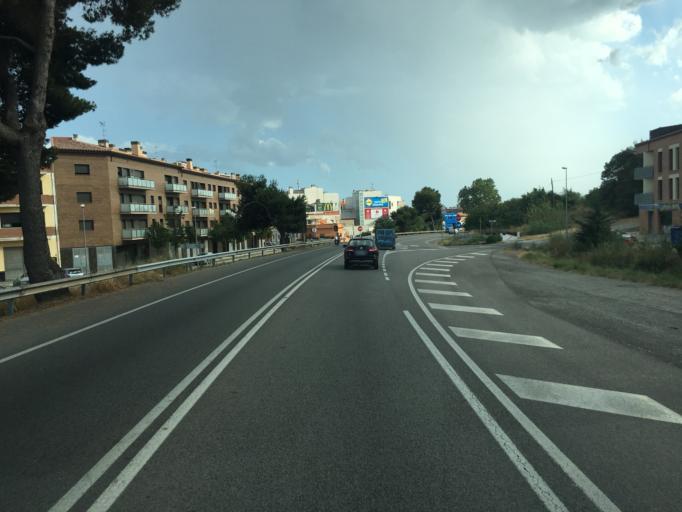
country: ES
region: Catalonia
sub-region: Provincia de Barcelona
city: Malgrat de Mar
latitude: 41.6512
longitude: 2.7354
